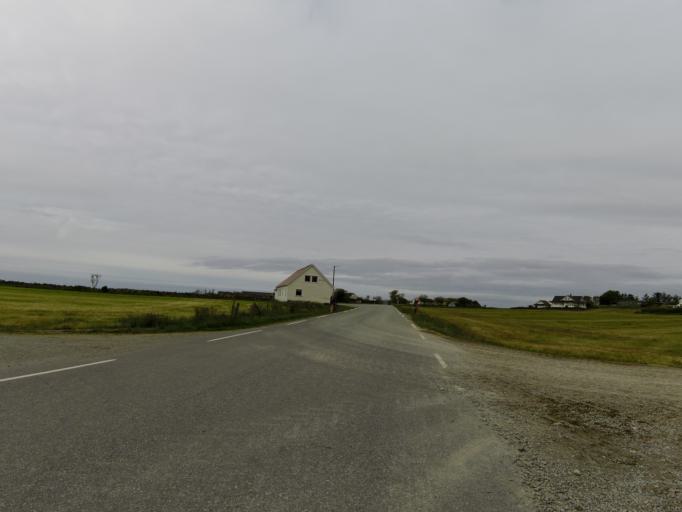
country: NO
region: Rogaland
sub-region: Klepp
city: Kleppe
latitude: 58.8168
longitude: 5.5724
